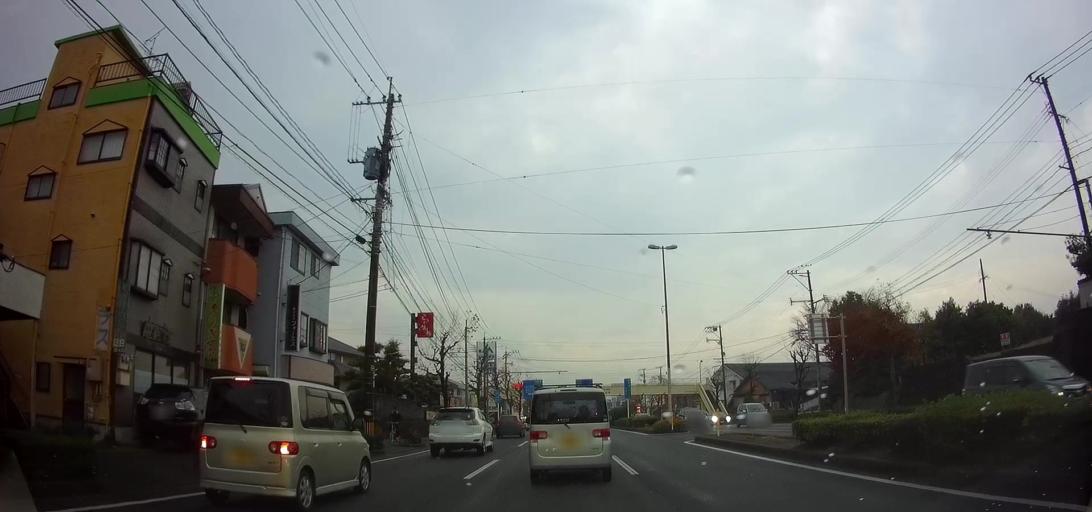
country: JP
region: Nagasaki
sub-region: Isahaya-shi
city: Isahaya
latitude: 32.8374
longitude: 130.0179
